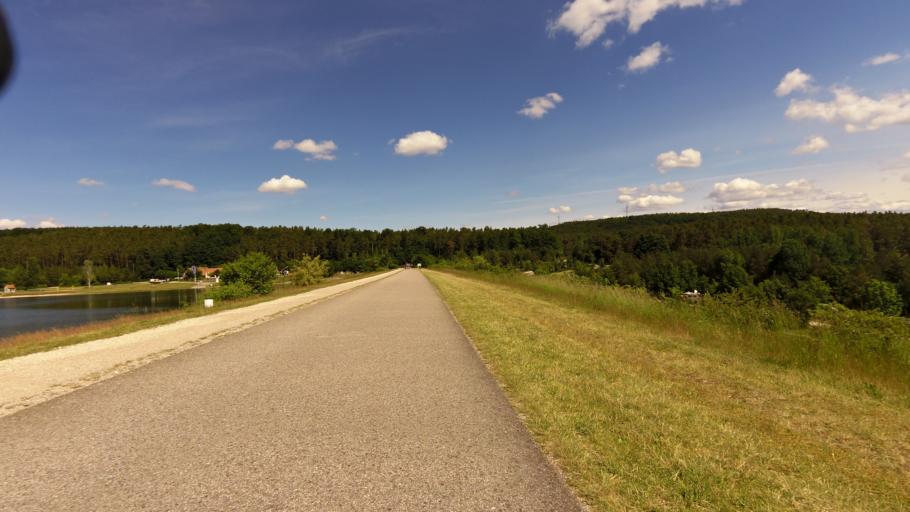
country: DE
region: Bavaria
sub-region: Regierungsbezirk Mittelfranken
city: Pleinfeld
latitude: 49.1316
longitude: 10.9623
